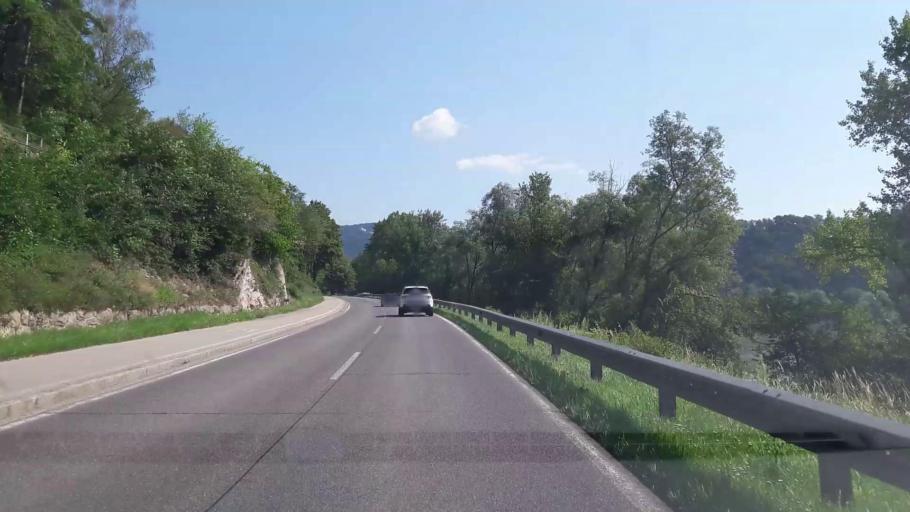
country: AT
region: Lower Austria
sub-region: Politischer Bezirk Krems
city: Aggsbach
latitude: 48.2835
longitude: 15.3976
